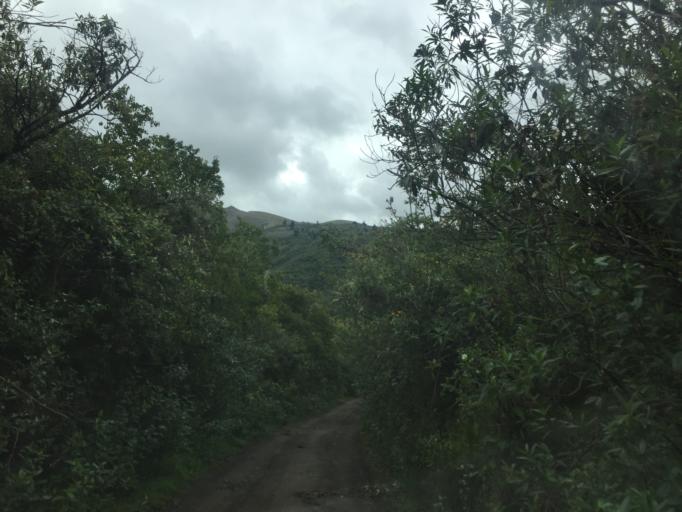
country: EC
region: Pichincha
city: Cayambe
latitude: 0.0758
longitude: -78.2994
